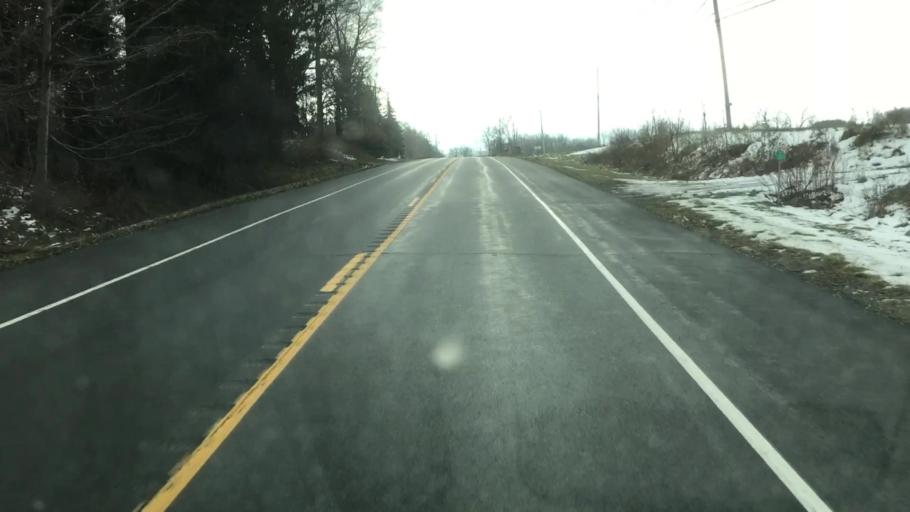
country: US
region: New York
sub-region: Onondaga County
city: Skaneateles
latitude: 42.8945
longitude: -76.4175
